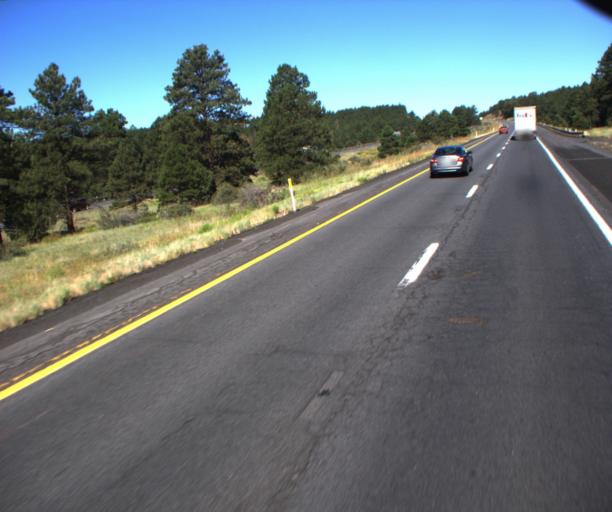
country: US
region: Arizona
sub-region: Coconino County
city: Parks
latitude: 35.2514
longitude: -111.9954
